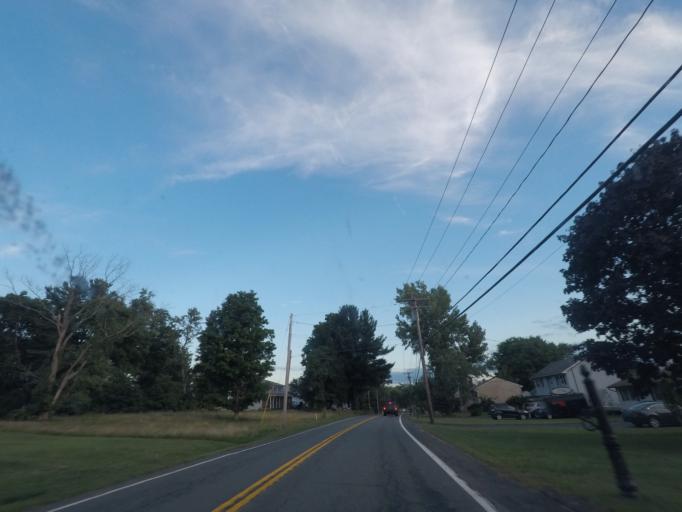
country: US
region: New York
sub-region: Schenectady County
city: Niskayuna
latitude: 42.7755
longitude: -73.7852
